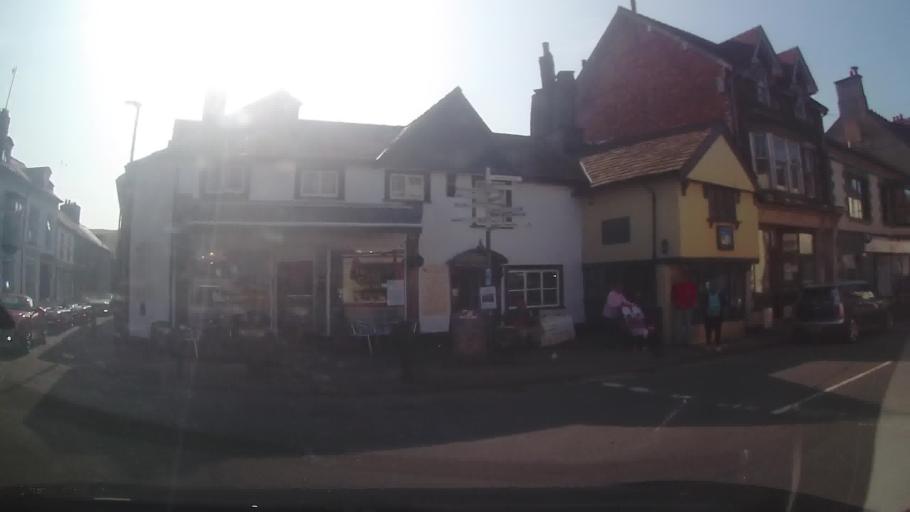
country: GB
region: Wales
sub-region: Sir Powys
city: Rhayader
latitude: 52.3004
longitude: -3.5105
